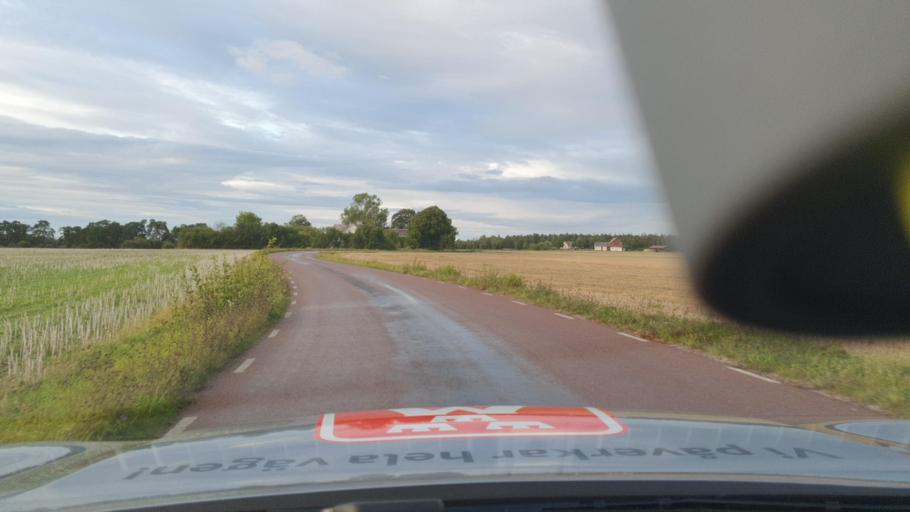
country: SE
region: Gotland
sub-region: Gotland
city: Visby
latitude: 57.6003
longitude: 18.4538
